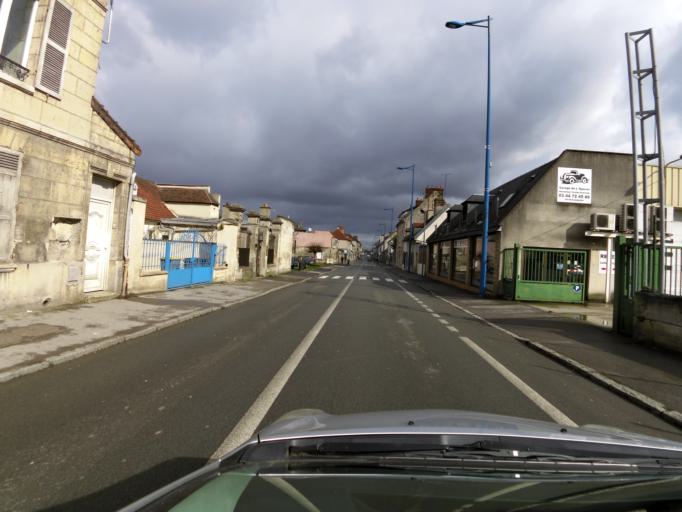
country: FR
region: Picardie
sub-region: Departement de l'Oise
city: Pont-Sainte-Maxence
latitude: 49.2989
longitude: 2.6045
